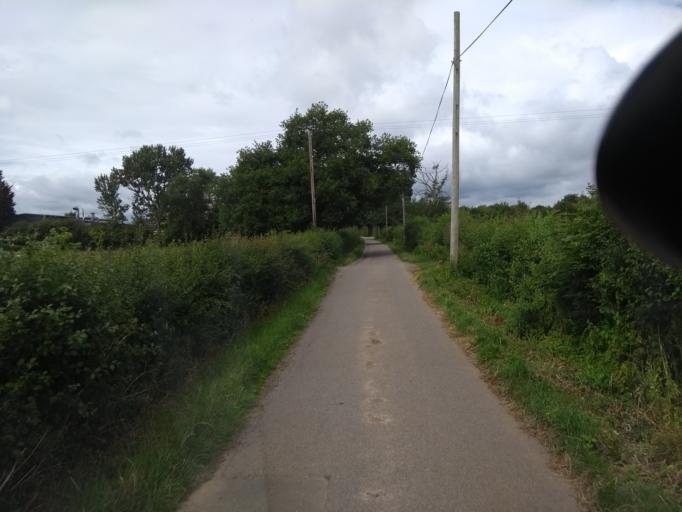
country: GB
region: England
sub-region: Somerset
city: Curry Rivel
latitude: 50.9950
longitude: -2.9191
